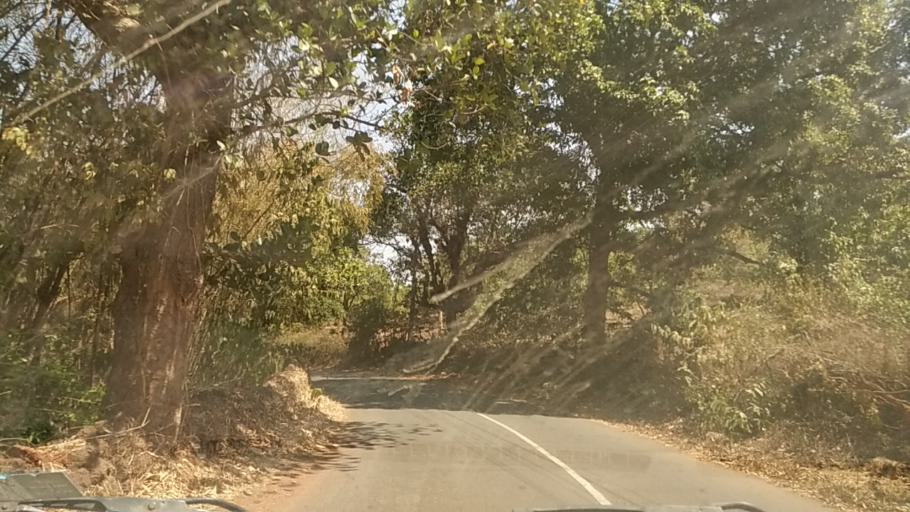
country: IN
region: Goa
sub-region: North Goa
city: Dicholi
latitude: 15.5762
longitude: 73.9150
